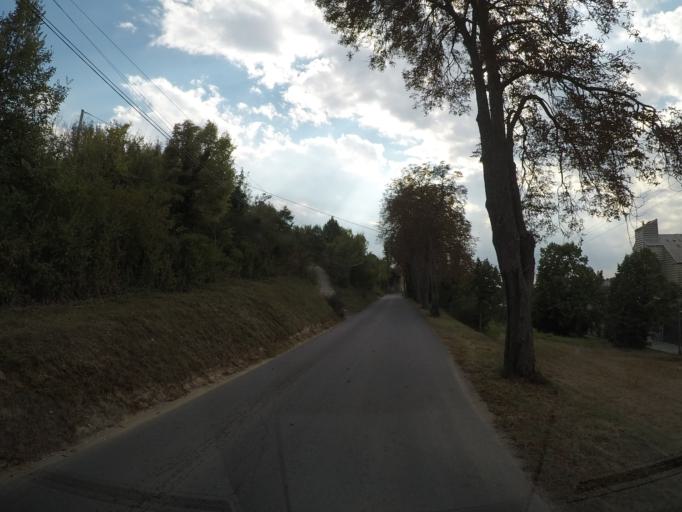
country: FR
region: Provence-Alpes-Cote d'Azur
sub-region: Departement des Alpes-de-Haute-Provence
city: Valensole
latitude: 43.8377
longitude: 5.9910
